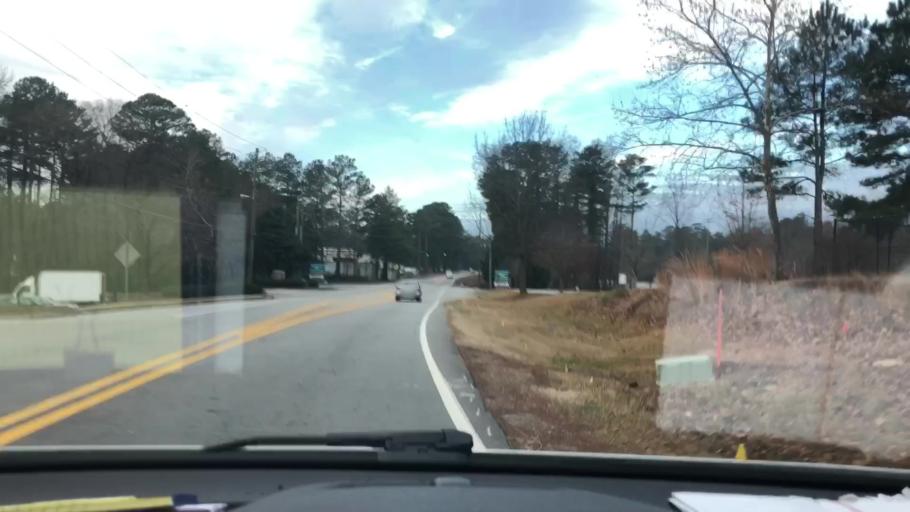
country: US
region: Georgia
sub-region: Gwinnett County
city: Berkeley Lake
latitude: 33.9671
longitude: -84.1854
